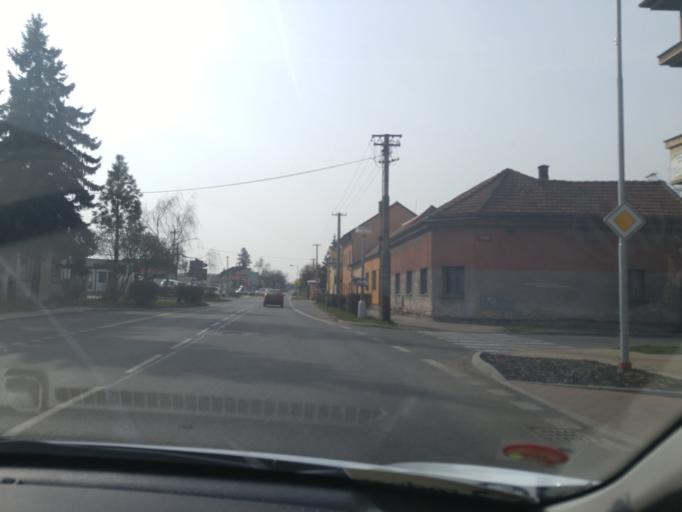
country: CZ
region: Central Bohemia
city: Kostelec nad Labem
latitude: 50.2249
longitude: 14.5844
